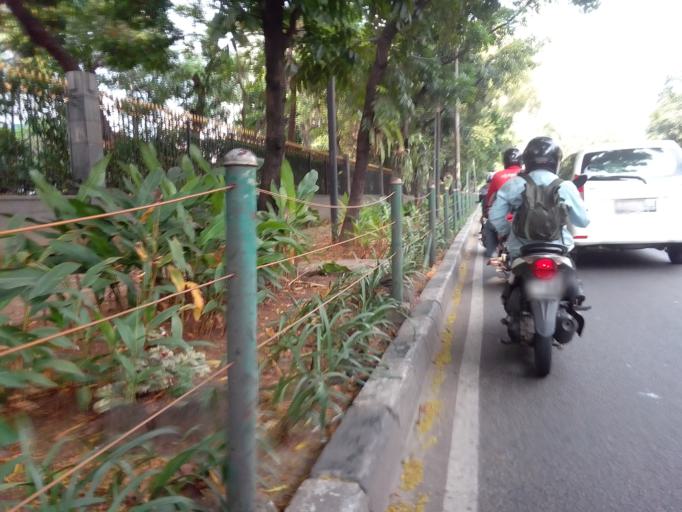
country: ID
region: Jakarta Raya
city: Jakarta
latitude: -6.1830
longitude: 106.8204
